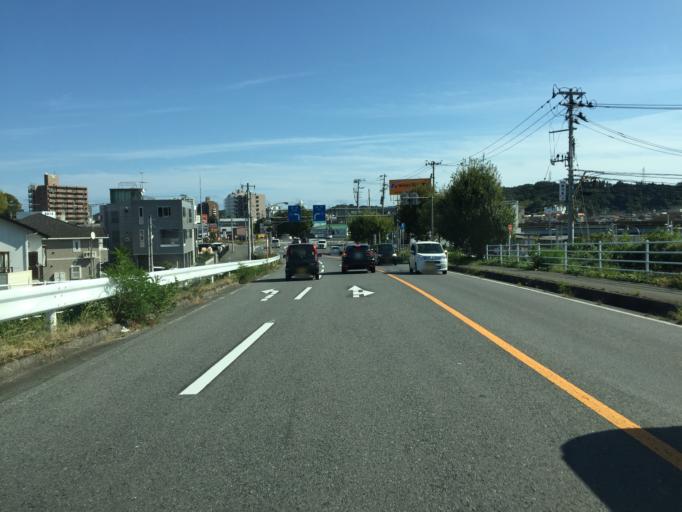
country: JP
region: Fukushima
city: Iwaki
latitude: 37.0540
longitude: 140.8780
